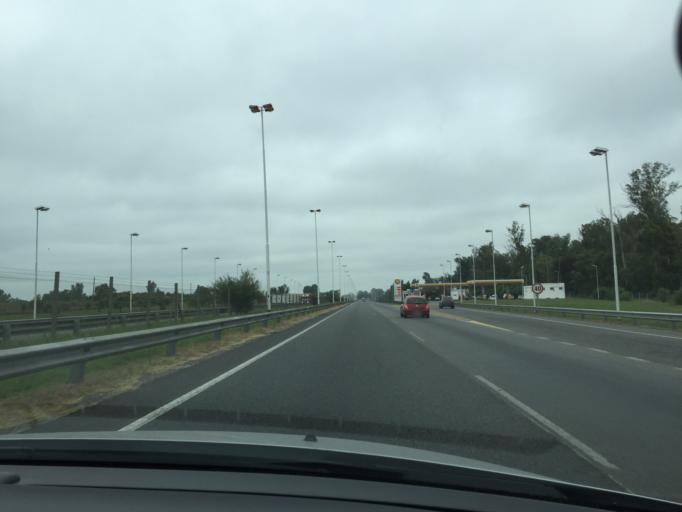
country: AR
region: Buenos Aires
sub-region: Partido de Ezeiza
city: Ezeiza
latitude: -34.8592
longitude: -58.5620
